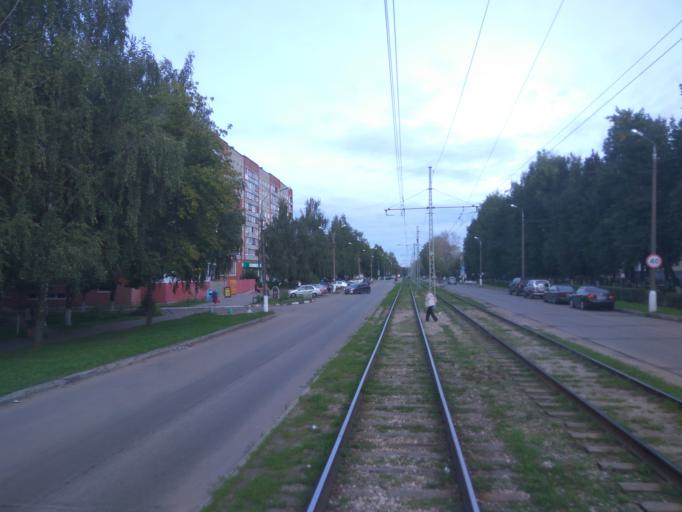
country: RU
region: Moskovskaya
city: Kolomna
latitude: 55.0777
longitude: 38.7733
